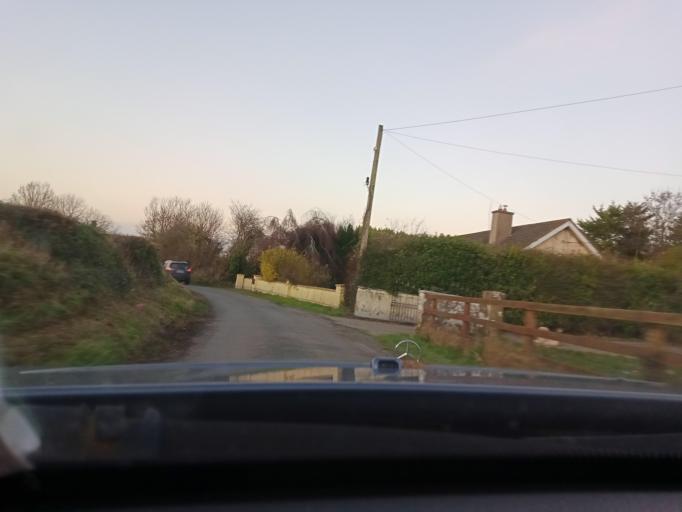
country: IE
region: Munster
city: Carrick-on-Suir
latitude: 52.4358
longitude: -7.3934
